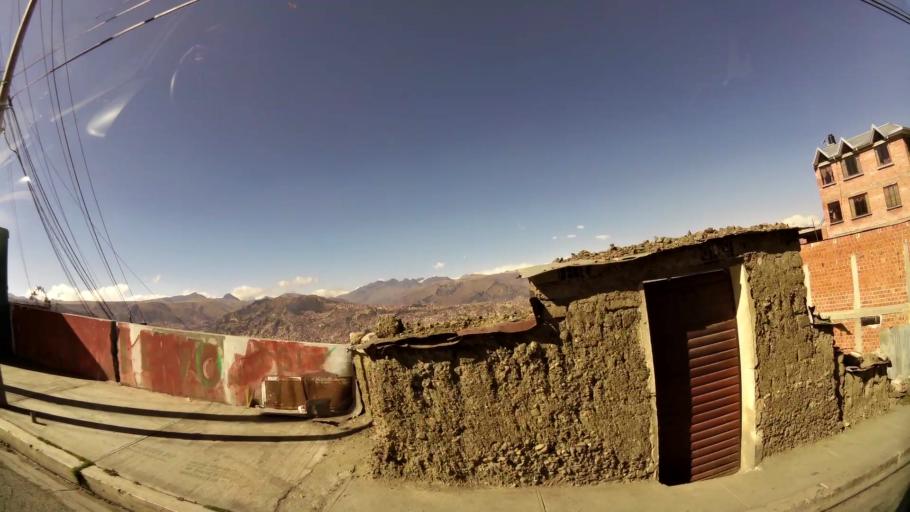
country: BO
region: La Paz
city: La Paz
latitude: -16.5188
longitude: -68.1418
